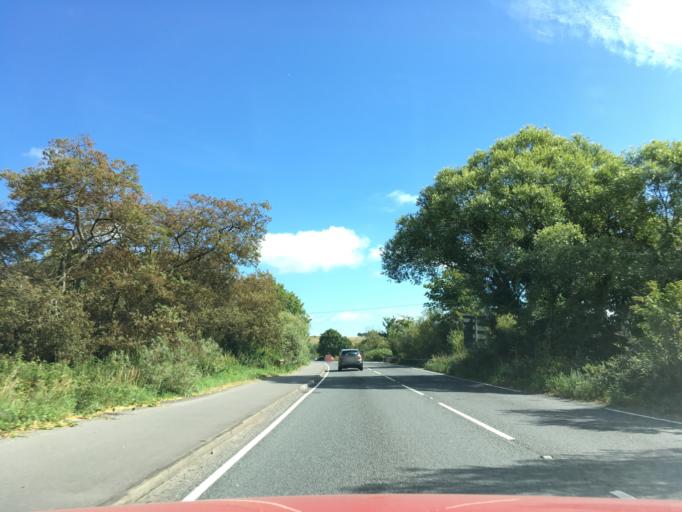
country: GB
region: England
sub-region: Dorset
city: Dorchester
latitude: 50.7267
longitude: -2.4604
